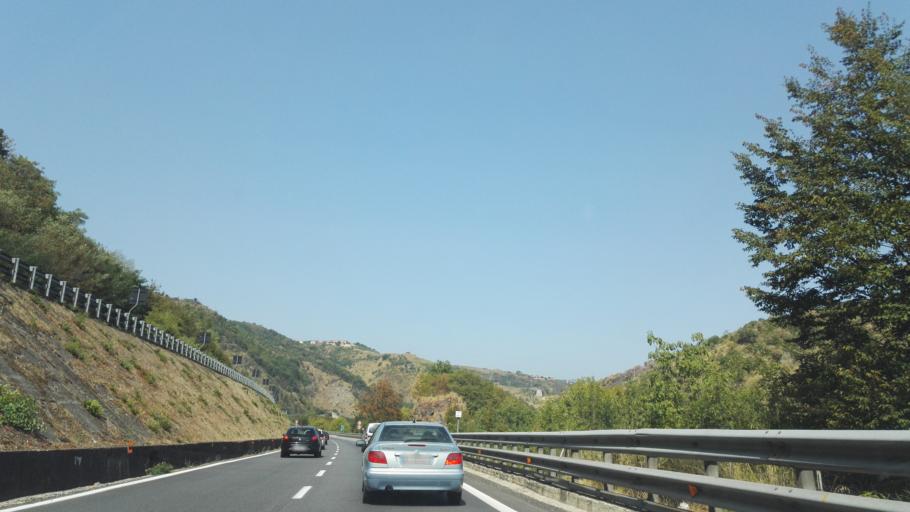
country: IT
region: Calabria
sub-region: Provincia di Cosenza
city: Dipignano
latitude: 39.2565
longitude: 16.2675
